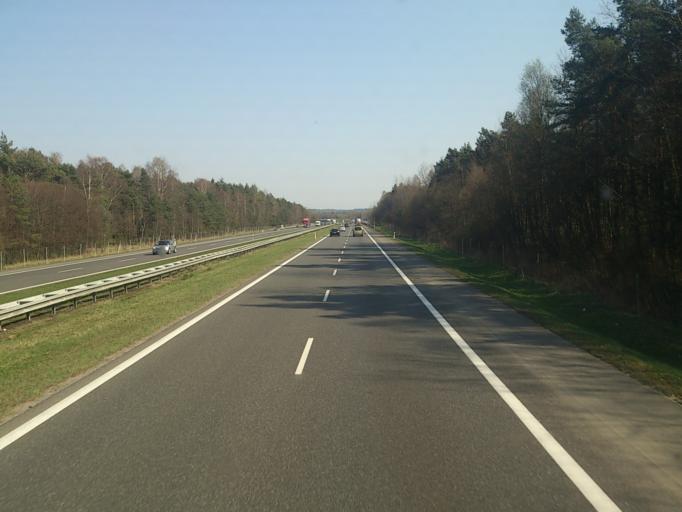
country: PL
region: Lesser Poland Voivodeship
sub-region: Powiat chrzanowski
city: Bolecin
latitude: 50.1177
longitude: 19.4990
